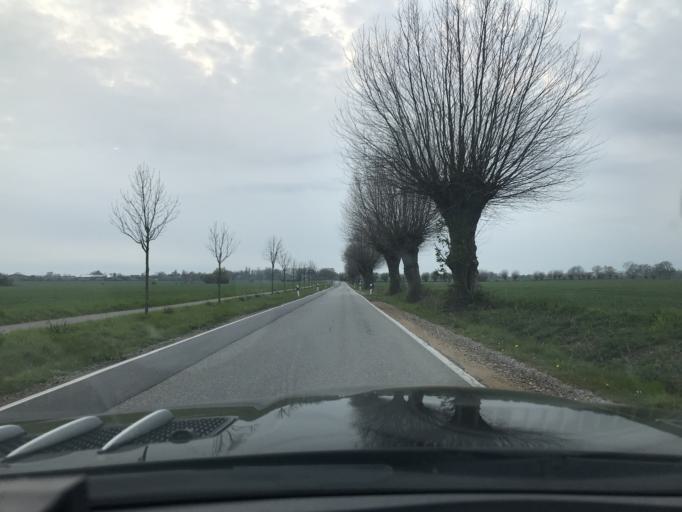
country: DE
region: Schleswig-Holstein
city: Burg auf Fehmarn
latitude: 54.4254
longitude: 11.2424
